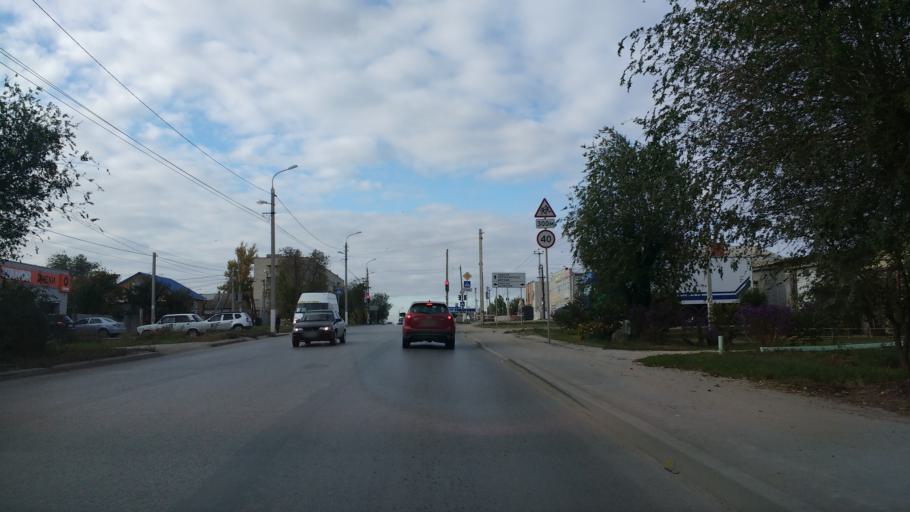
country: RU
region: Volgograd
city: Volgograd
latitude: 48.7655
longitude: 44.5303
